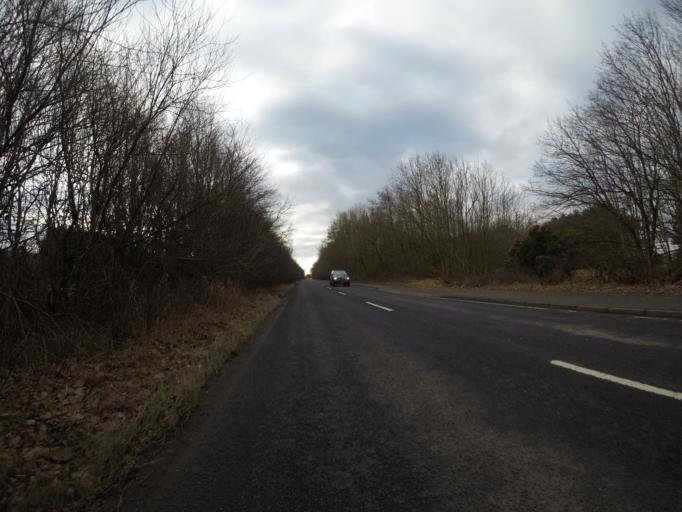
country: GB
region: Scotland
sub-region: North Ayrshire
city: Dreghorn
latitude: 55.5810
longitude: -4.6443
